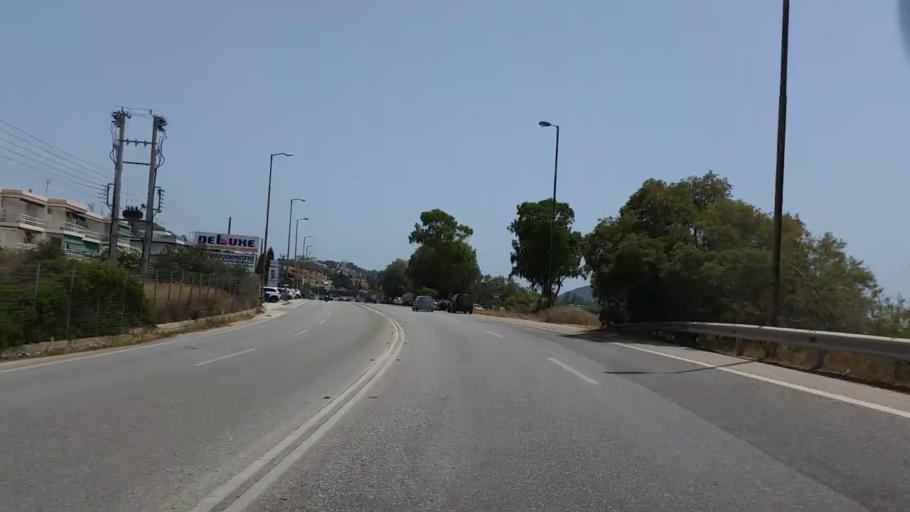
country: GR
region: Attica
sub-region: Nomarchia Anatolikis Attikis
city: Saronida
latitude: 37.7397
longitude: 23.9046
